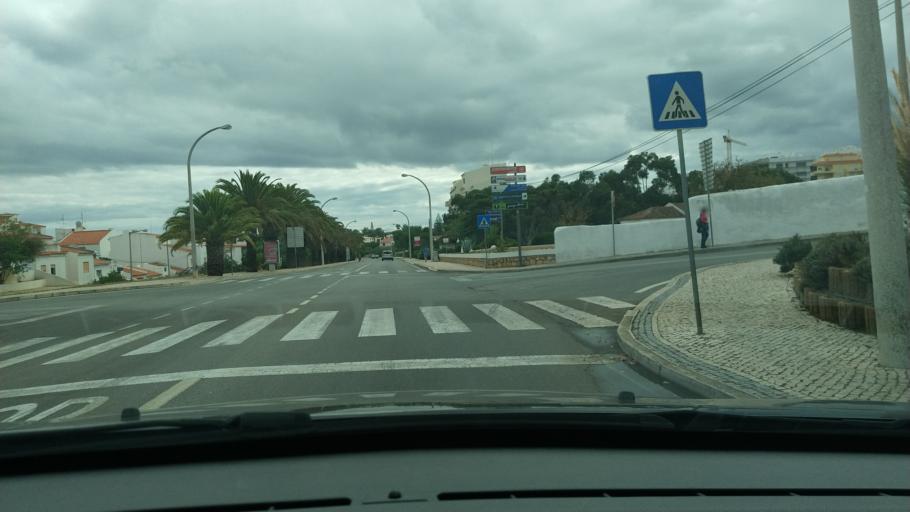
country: PT
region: Faro
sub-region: Lagos
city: Lagos
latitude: 37.0981
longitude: -8.6790
